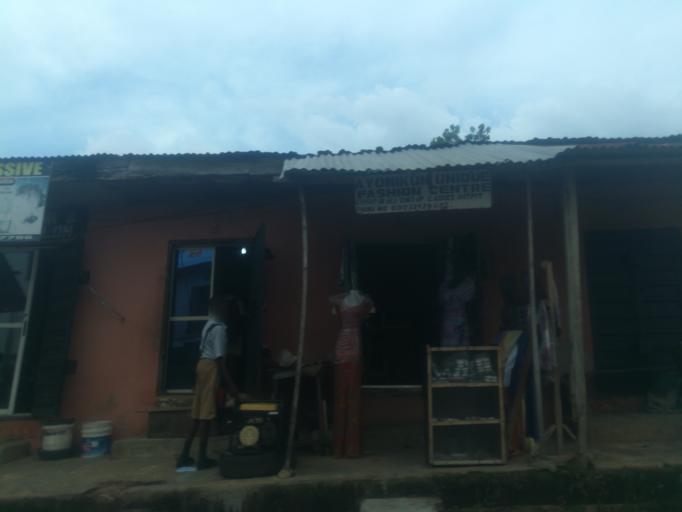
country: NG
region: Oyo
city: Ibadan
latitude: 7.3778
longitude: 3.8259
